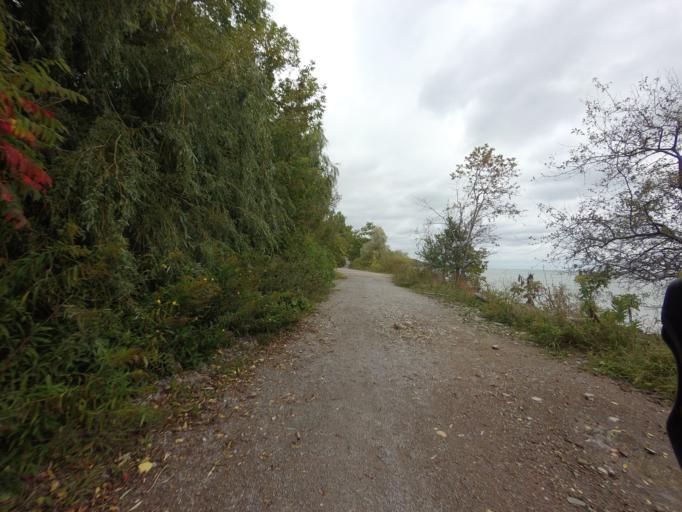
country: CA
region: Ontario
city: Scarborough
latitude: 43.7449
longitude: -79.1912
